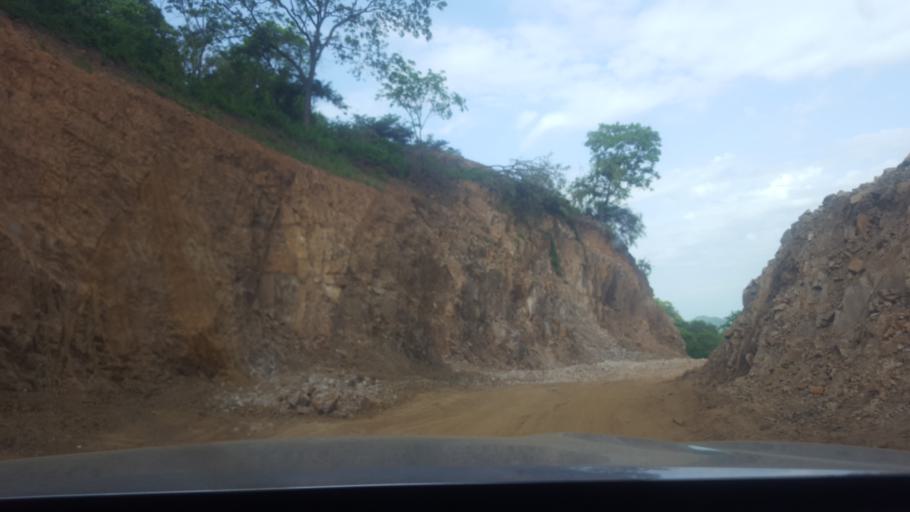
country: ET
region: Southern Nations, Nationalities, and People's Region
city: Tippi
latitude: 7.5373
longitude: 34.9732
